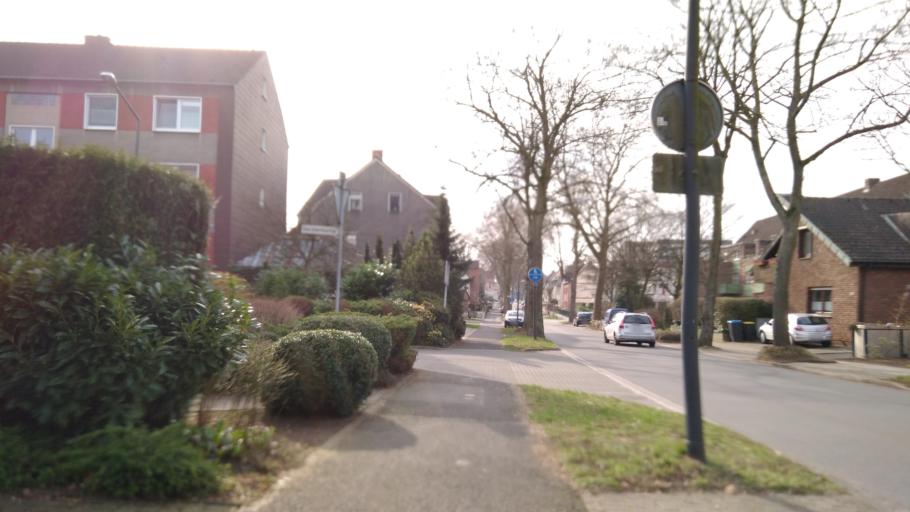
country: DE
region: North Rhine-Westphalia
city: Herten
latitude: 51.6256
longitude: 7.1465
